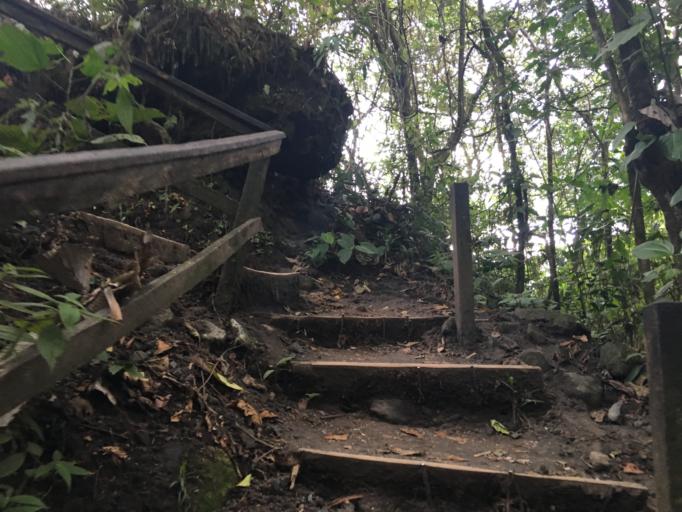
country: CR
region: Alajuela
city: La Fortuna
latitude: 10.4517
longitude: -84.7253
